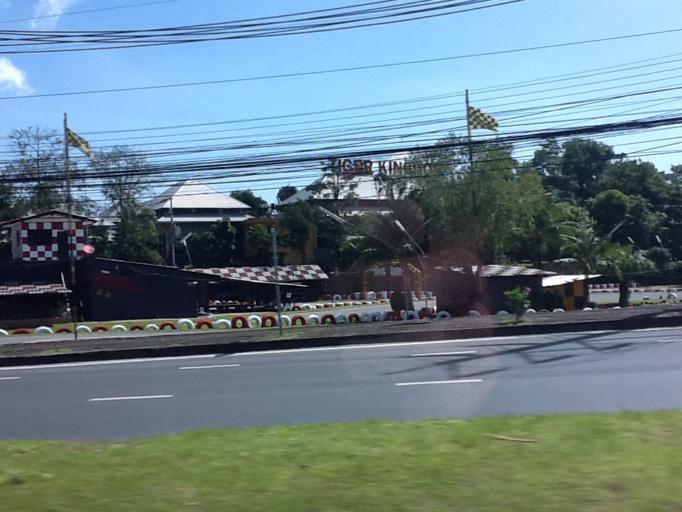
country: TH
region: Phuket
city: Kathu
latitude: 7.9069
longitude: 98.3289
